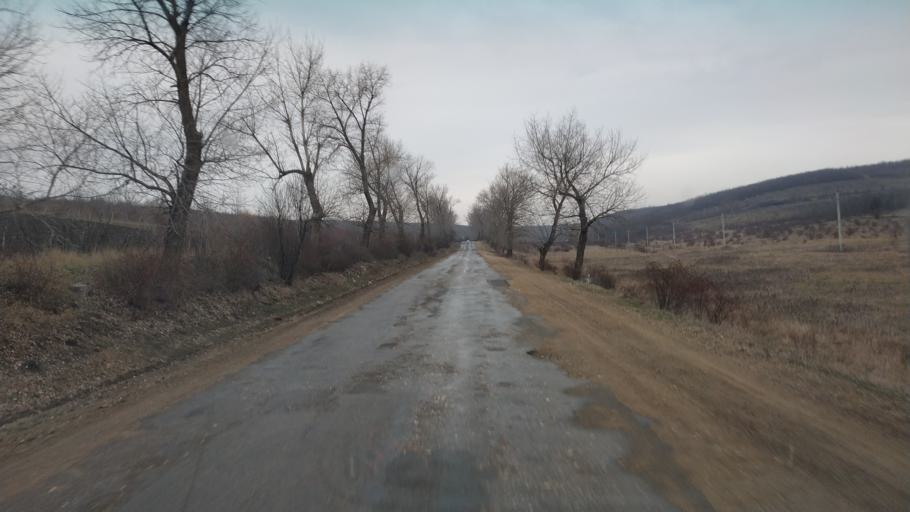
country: MD
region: Chisinau
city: Singera
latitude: 46.8426
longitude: 28.9813
